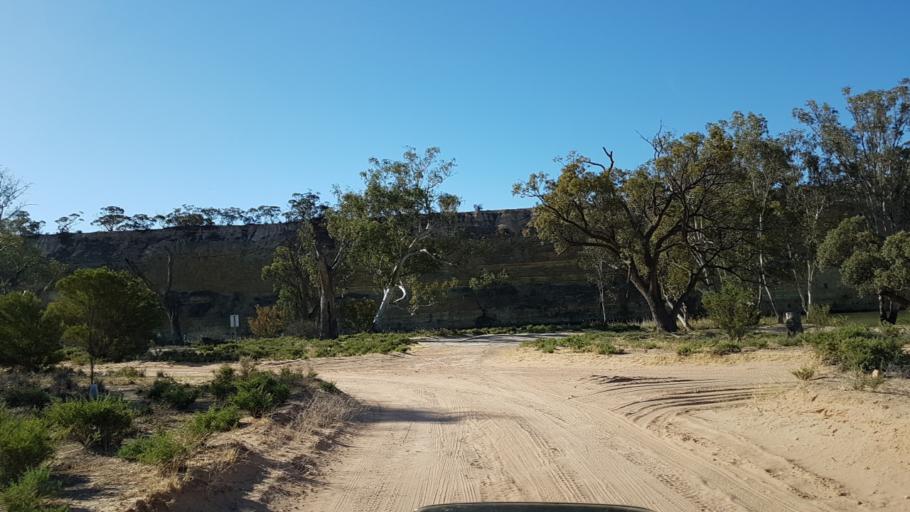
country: AU
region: South Australia
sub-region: Loxton Waikerie
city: Waikerie
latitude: -34.1553
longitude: 140.0217
